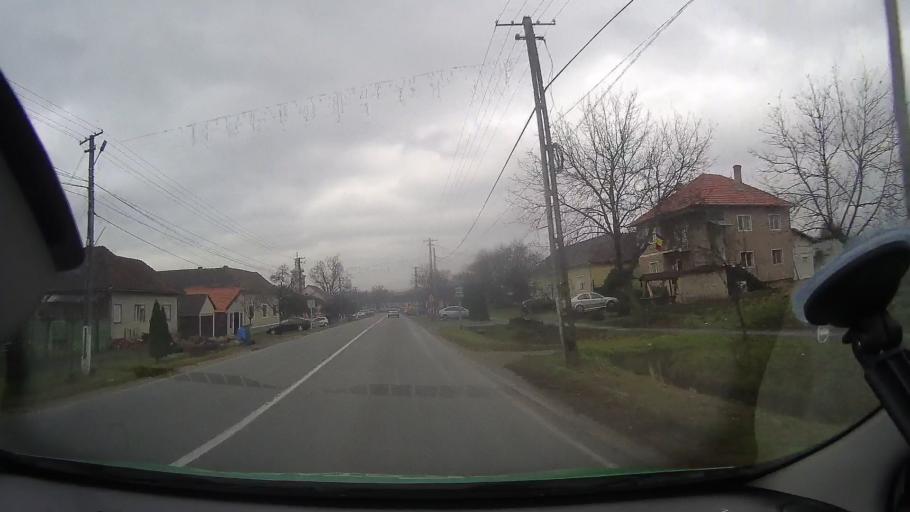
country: RO
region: Arad
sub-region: Comuna Almas
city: Almas
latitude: 46.2853
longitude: 22.2336
